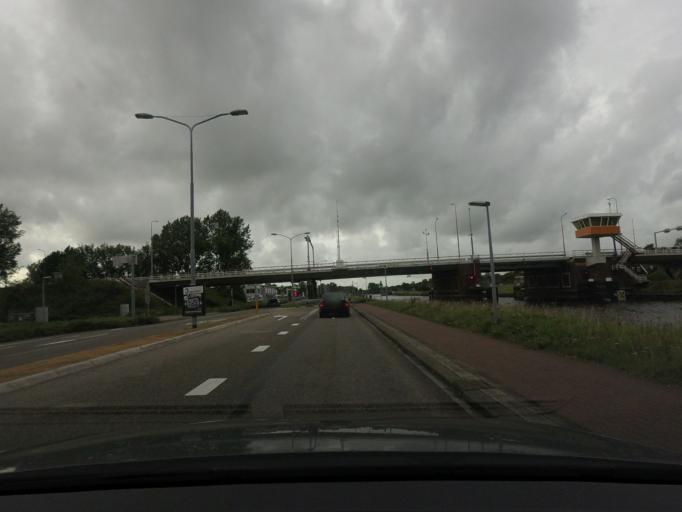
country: NL
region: North Holland
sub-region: Gemeente Alkmaar
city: Alkmaar
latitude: 52.6459
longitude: 4.7436
